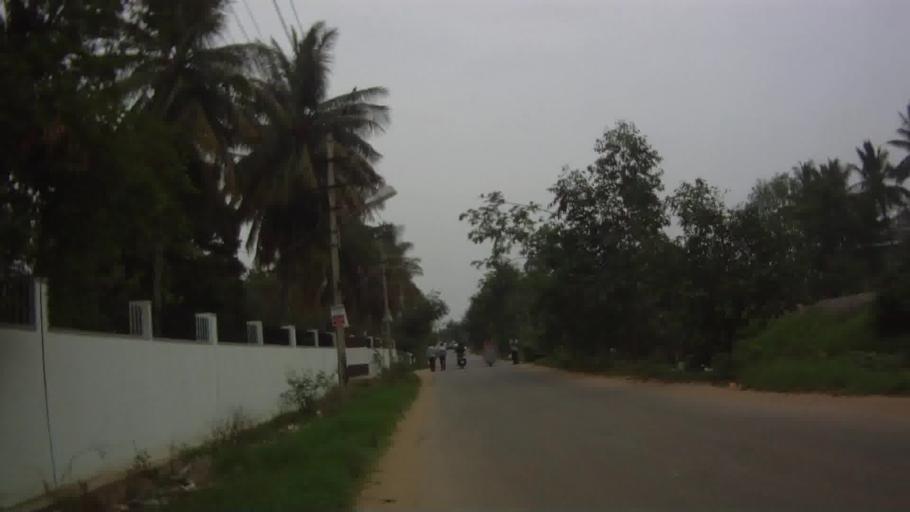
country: IN
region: Karnataka
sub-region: Bangalore Urban
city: Bangalore
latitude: 12.9647
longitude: 77.7037
